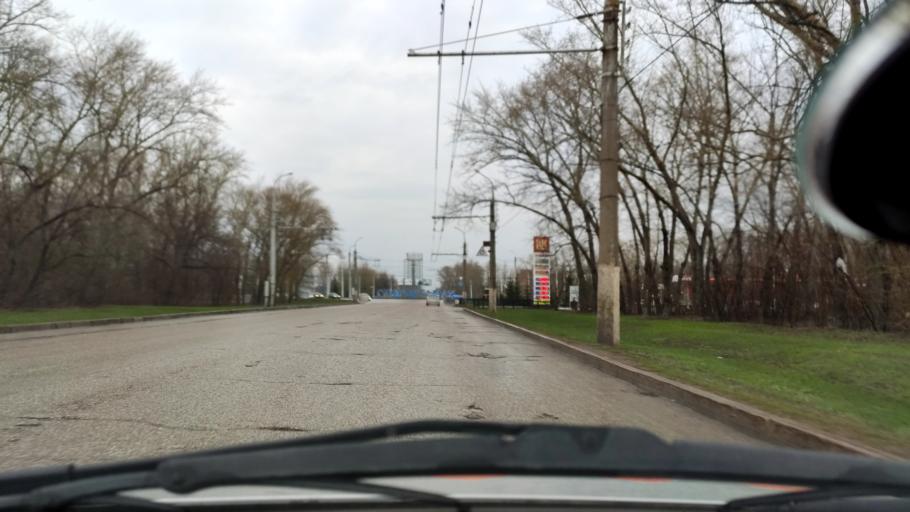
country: RU
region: Bashkortostan
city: Sterlitamak
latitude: 53.6615
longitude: 55.9490
